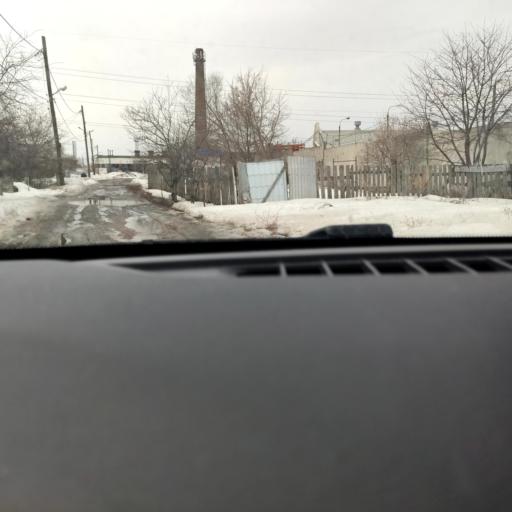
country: RU
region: Samara
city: Petra-Dubrava
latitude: 53.2578
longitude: 50.3156
